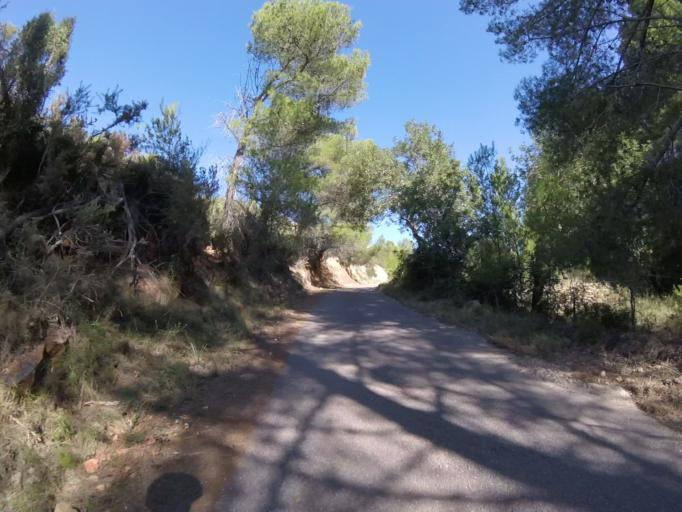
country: ES
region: Valencia
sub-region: Provincia de Castello
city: Cabanes
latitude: 40.1420
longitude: 0.1026
